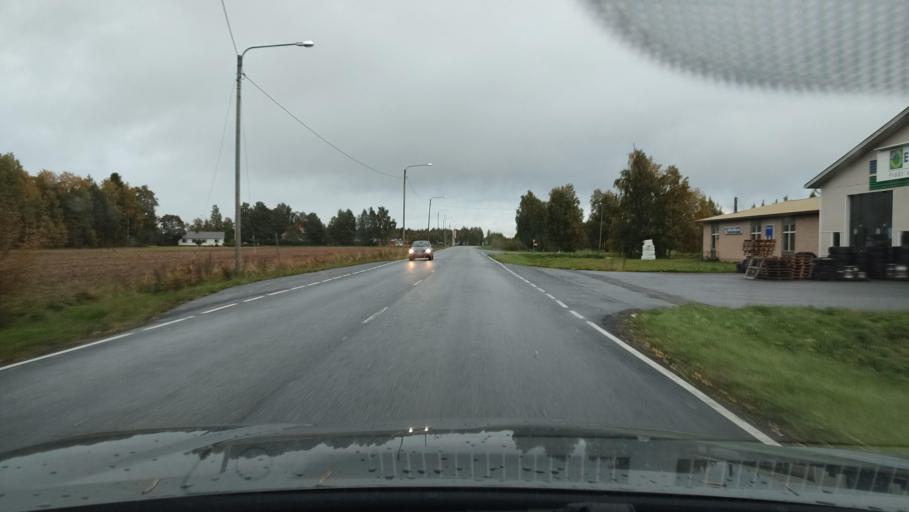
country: FI
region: Ostrobothnia
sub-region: Sydosterbotten
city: Kristinestad
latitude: 62.2653
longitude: 21.4785
